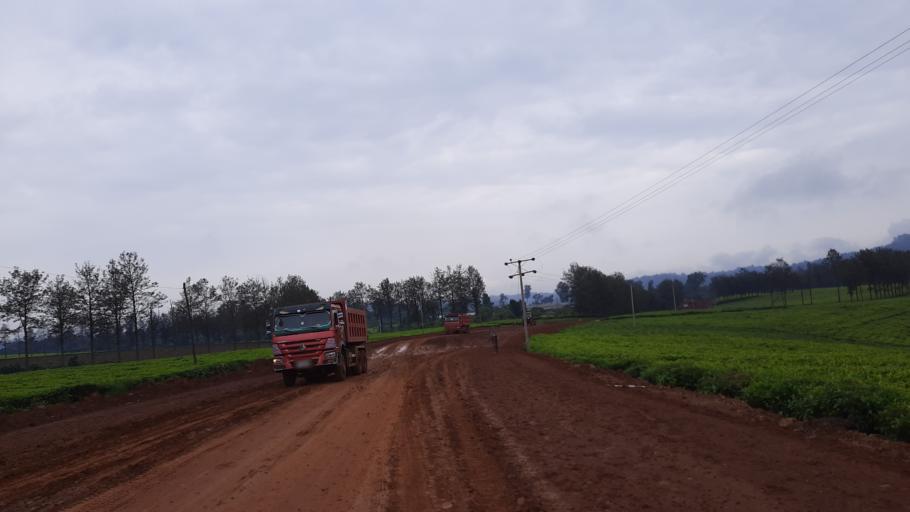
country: ET
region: Oromiya
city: Gore
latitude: 7.8556
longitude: 35.4755
